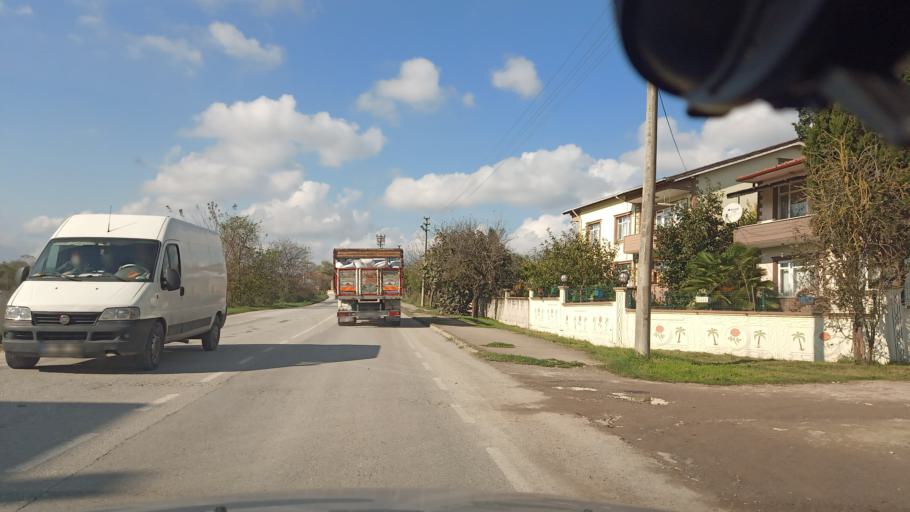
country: TR
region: Sakarya
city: Kaynarca
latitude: 41.0400
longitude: 30.2915
